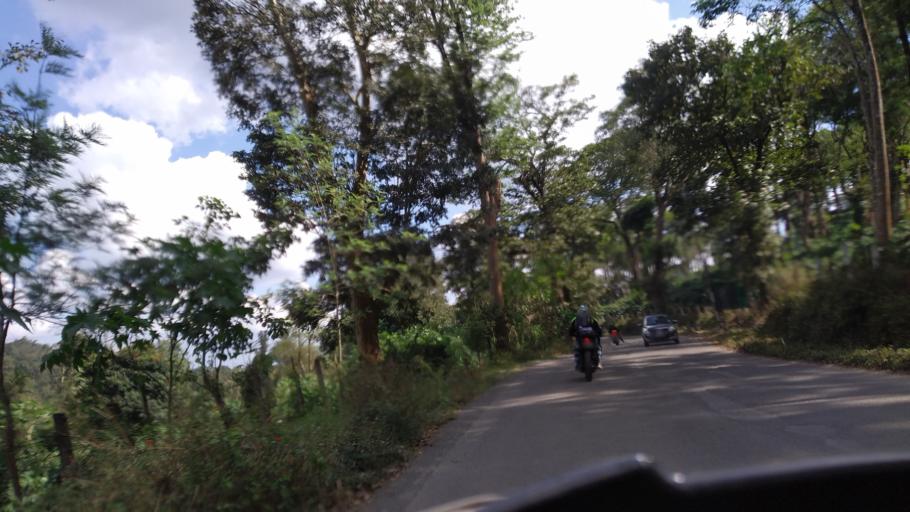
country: IN
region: Karnataka
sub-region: Kodagu
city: Ponnampet
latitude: 11.9614
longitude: 76.0600
